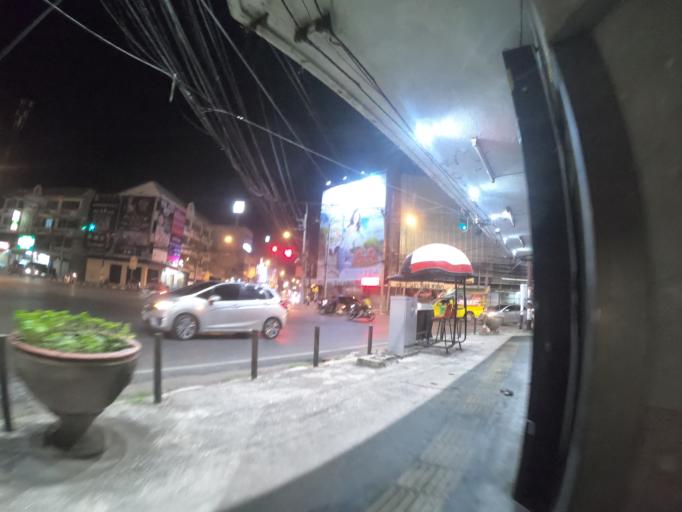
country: TH
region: Khon Kaen
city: Khon Kaen
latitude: 16.4304
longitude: 102.8353
